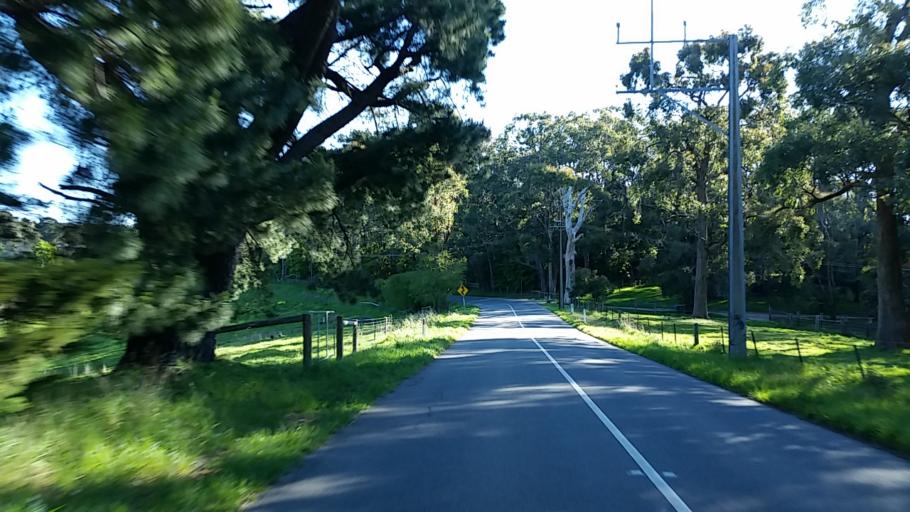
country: AU
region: South Australia
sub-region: Adelaide Hills
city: Adelaide Hills
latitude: -34.9339
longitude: 138.7437
